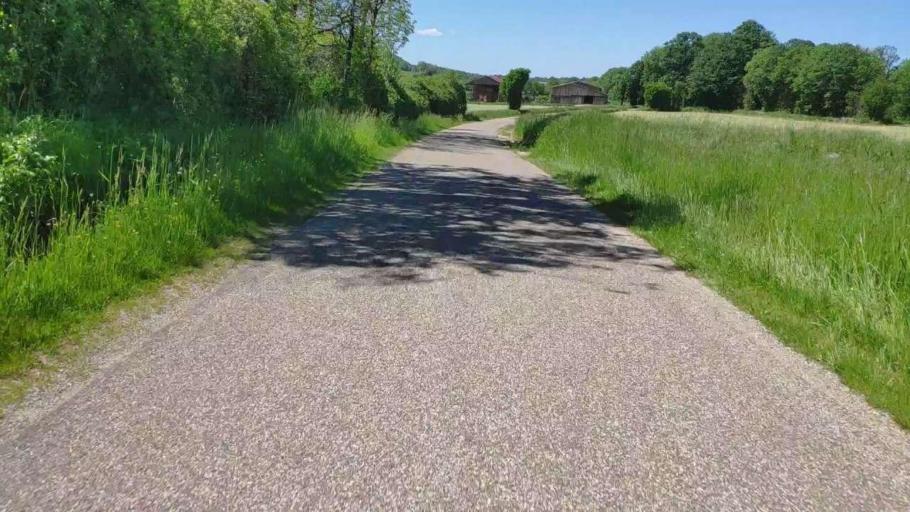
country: FR
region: Franche-Comte
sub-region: Departement du Jura
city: Poligny
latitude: 46.7313
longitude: 5.7548
